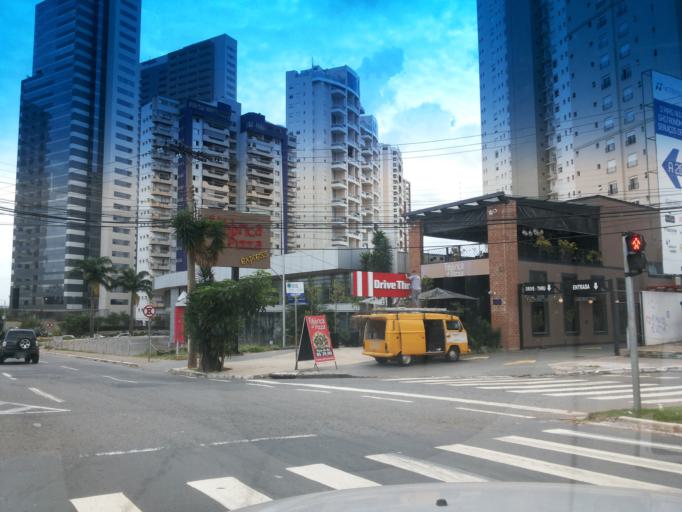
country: BR
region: Goias
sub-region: Goiania
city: Goiania
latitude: -16.7060
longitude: -49.2388
